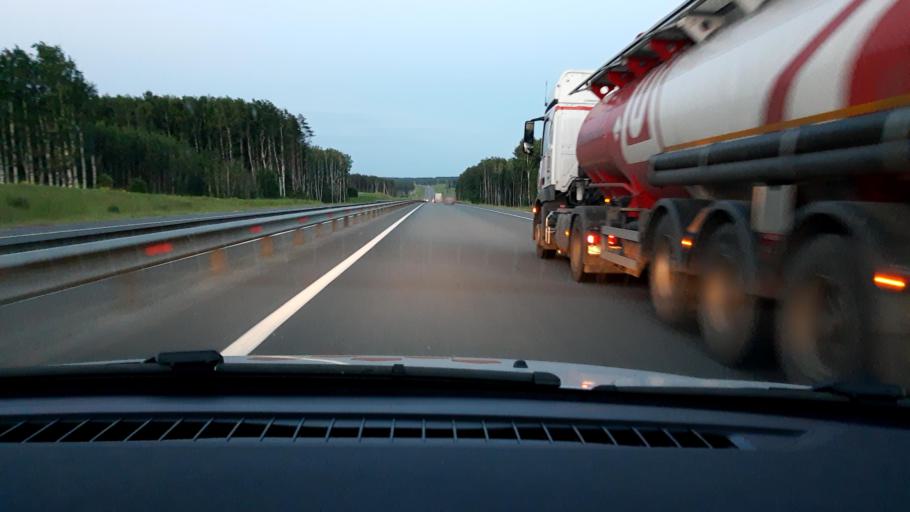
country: RU
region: Nizjnij Novgorod
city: Kstovo
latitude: 56.0880
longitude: 44.0865
